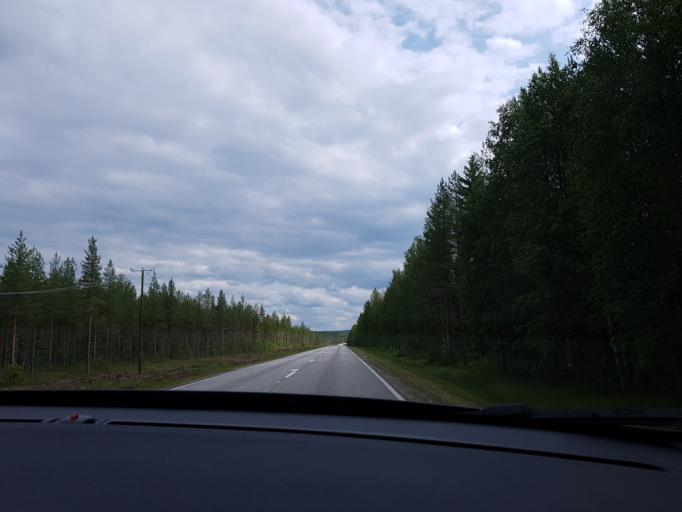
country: FI
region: Kainuu
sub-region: Kehys-Kainuu
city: Kuhmo
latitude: 64.3768
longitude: 29.8813
